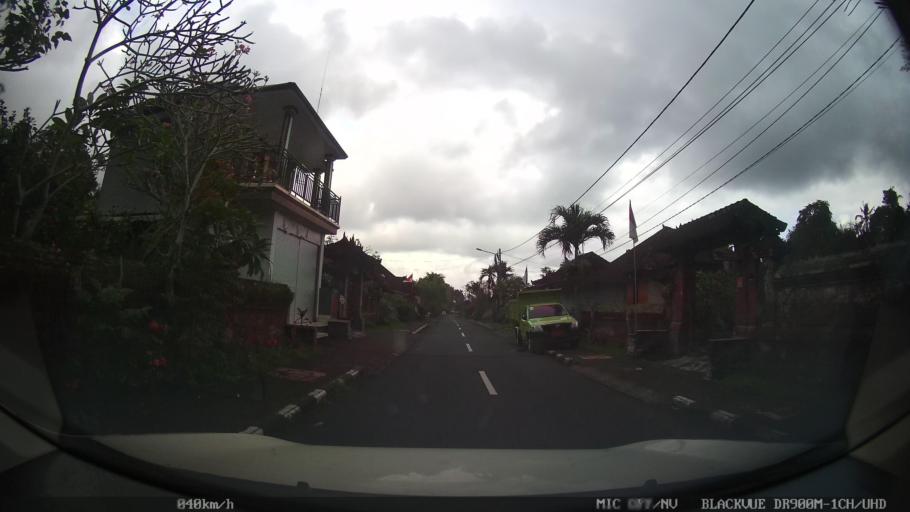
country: ID
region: Bali
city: Banjar Kembangsari
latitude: -8.5139
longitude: 115.2061
